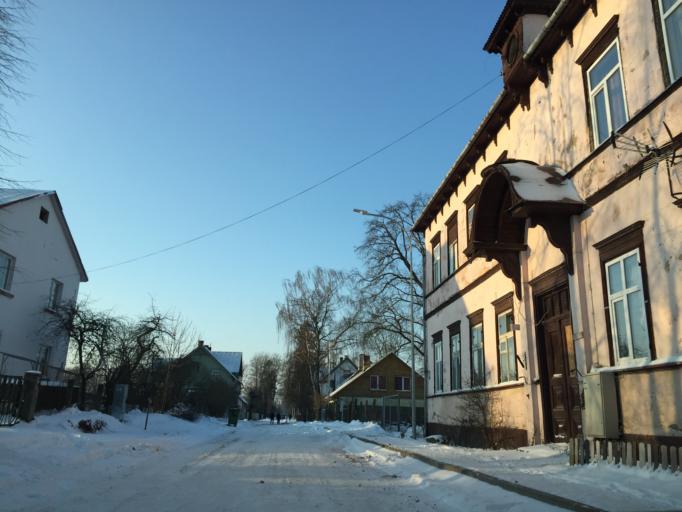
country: LV
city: Tireli
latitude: 56.9426
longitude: 23.6171
